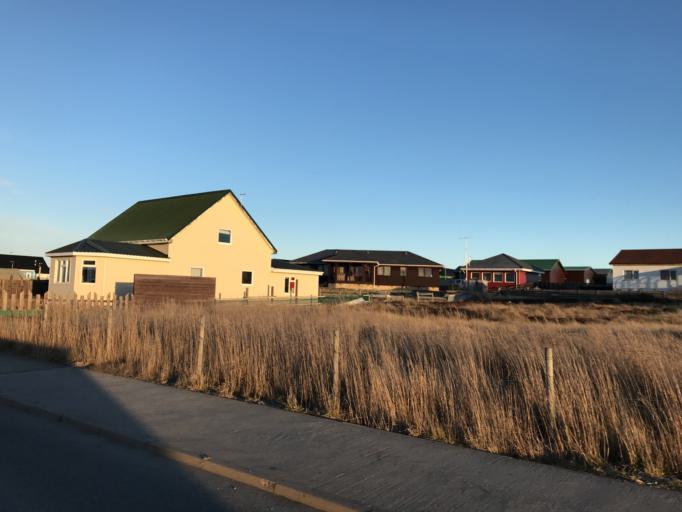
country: FK
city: Stanley
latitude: -51.6957
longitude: -57.8397
